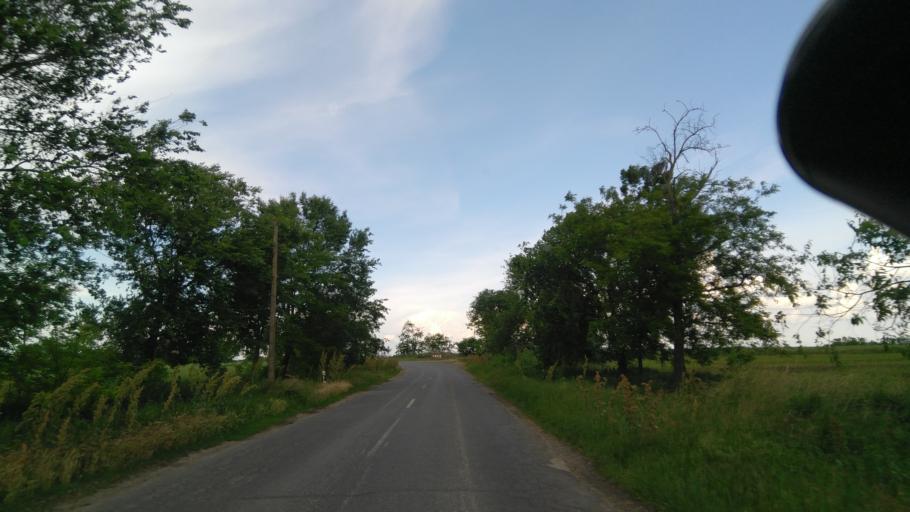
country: HU
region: Bekes
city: Dombegyhaz
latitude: 46.3539
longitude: 21.1638
